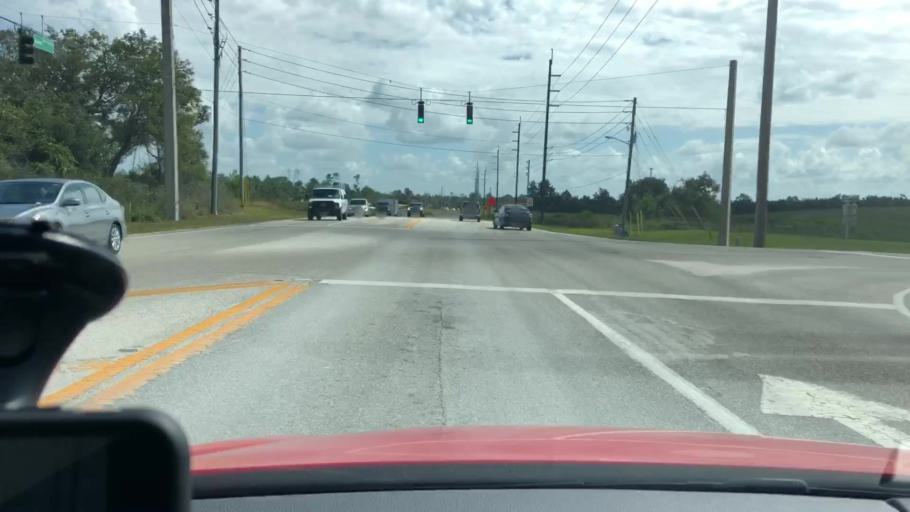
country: US
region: Florida
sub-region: Volusia County
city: Lake Helen
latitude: 28.9486
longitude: -81.2557
